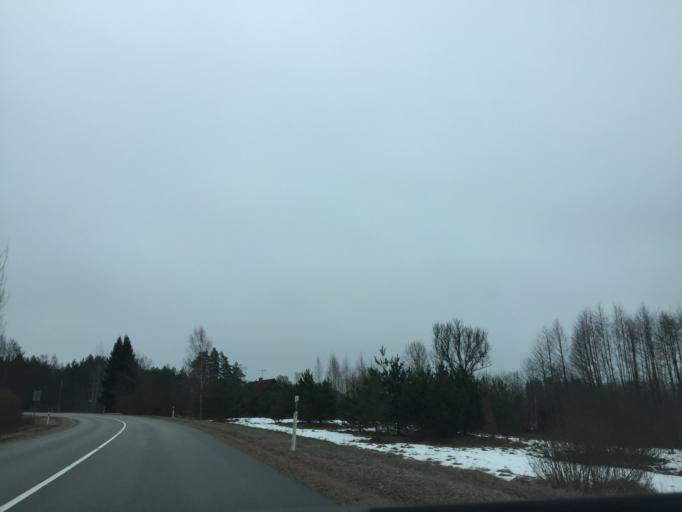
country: LV
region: Lecava
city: Iecava
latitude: 56.6072
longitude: 24.0445
